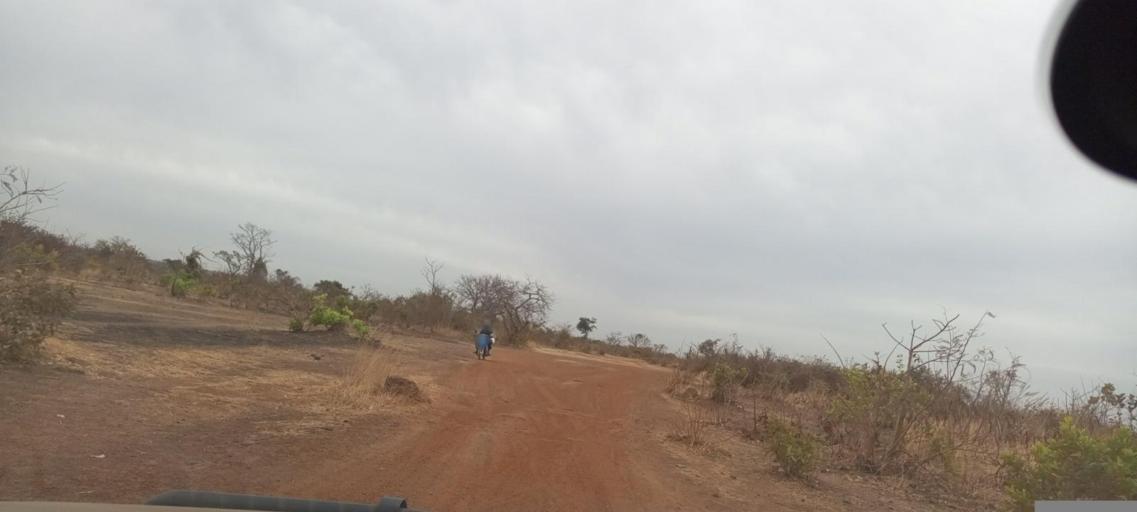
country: ML
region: Koulikoro
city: Kati
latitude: 12.7854
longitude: -8.2587
